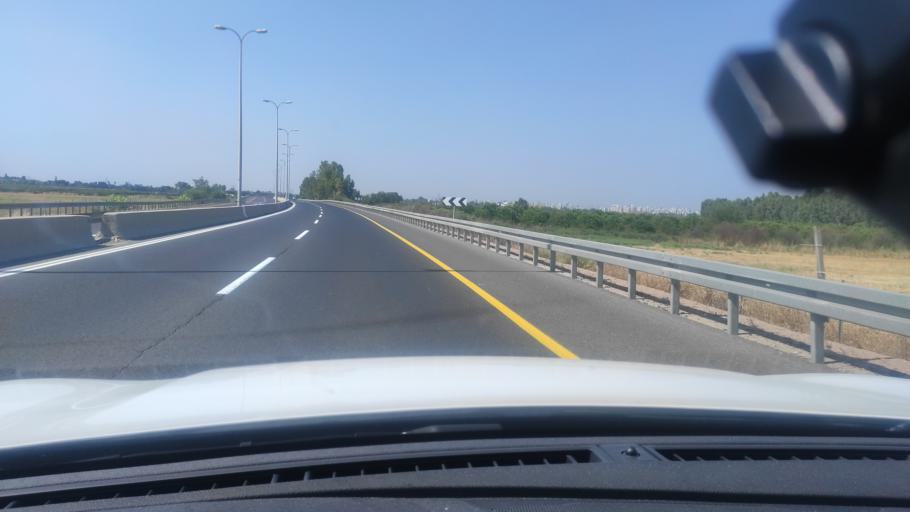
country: IL
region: Central District
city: Hod HaSharon
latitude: 32.1453
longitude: 34.9181
